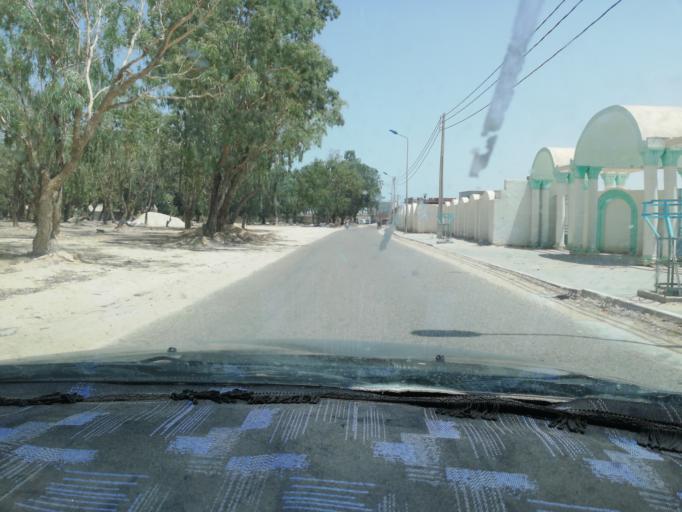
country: TN
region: Qabis
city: Matmata
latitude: 33.6204
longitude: 10.2779
